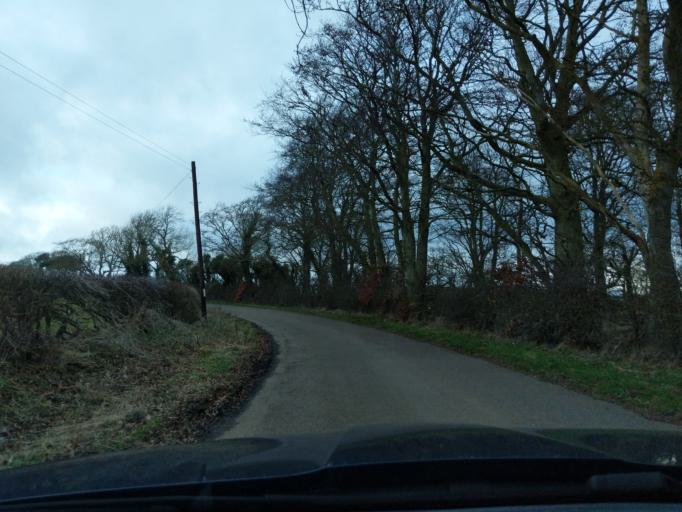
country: GB
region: England
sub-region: Northumberland
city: Ancroft
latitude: 55.7105
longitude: -2.0302
